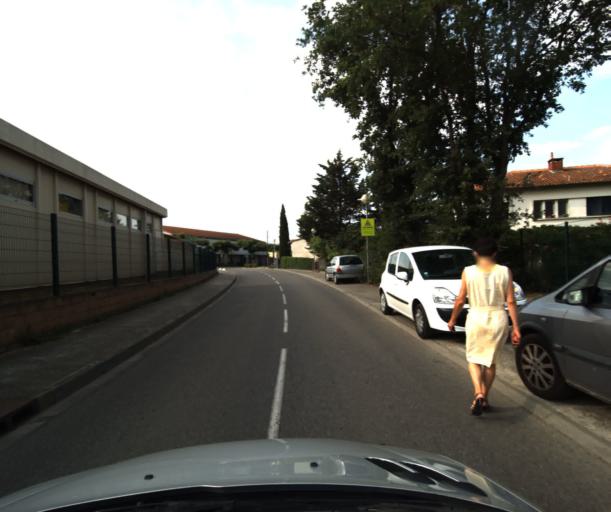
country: FR
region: Midi-Pyrenees
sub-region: Departement de la Haute-Garonne
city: Fonsorbes
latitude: 43.5324
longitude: 1.2315
